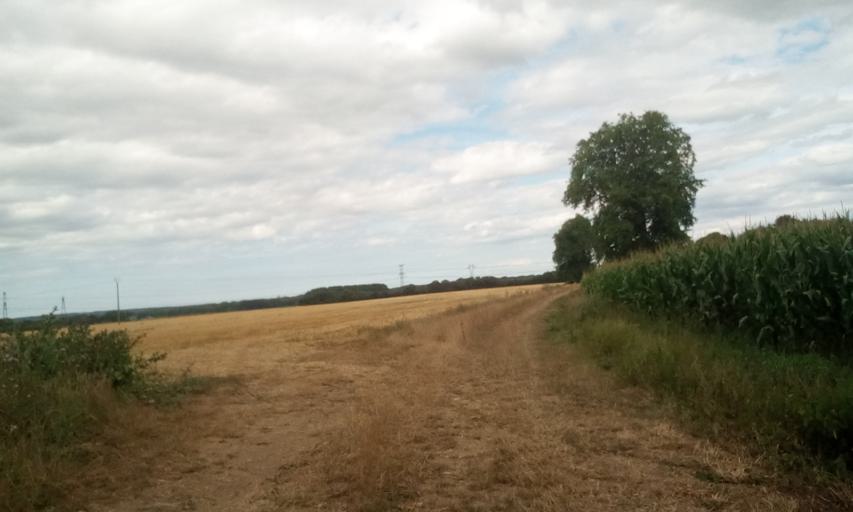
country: FR
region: Lower Normandy
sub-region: Departement du Calvados
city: Bellengreville
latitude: 49.1251
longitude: -0.2022
